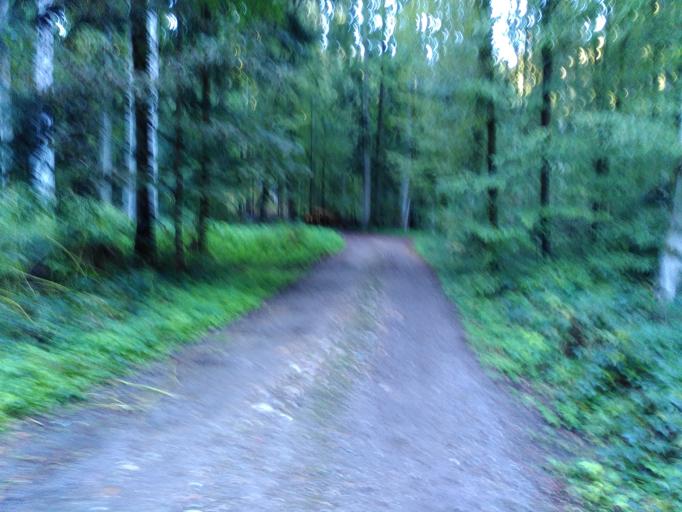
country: CH
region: Bern
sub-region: Emmental District
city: Ersigen
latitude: 47.0975
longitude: 7.6202
